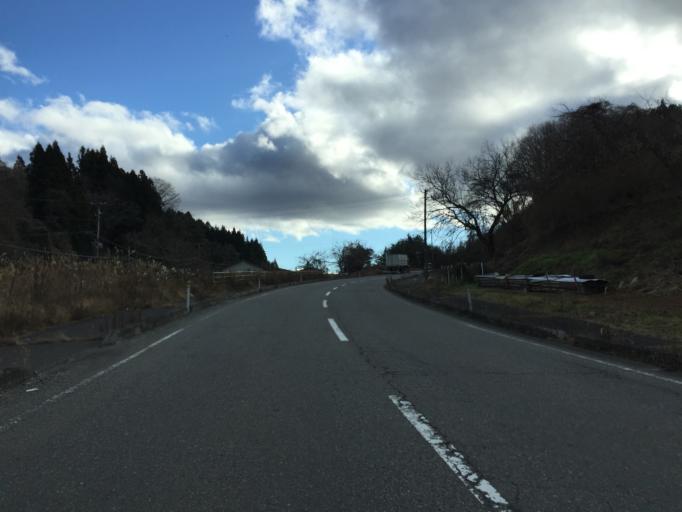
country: JP
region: Fukushima
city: Funehikimachi-funehiki
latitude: 37.5596
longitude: 140.5791
